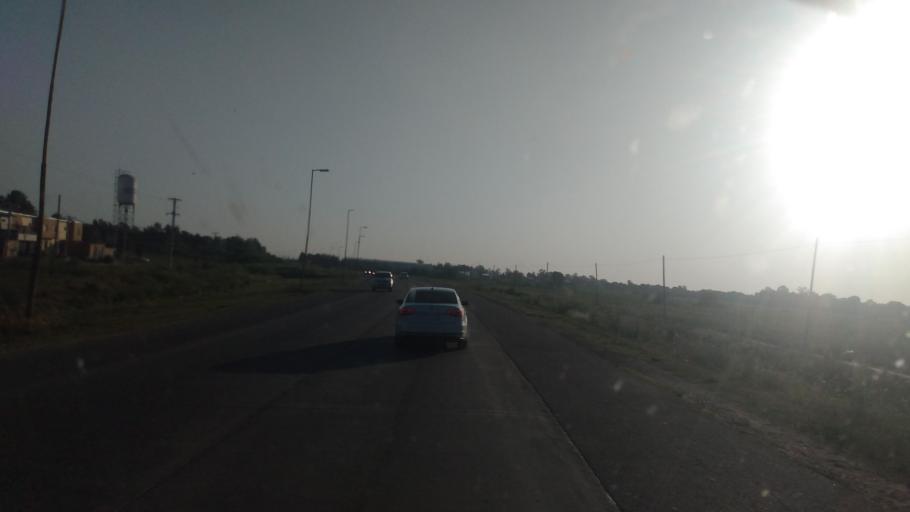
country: AR
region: Buenos Aires
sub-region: Partido de Campana
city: Campana
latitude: -34.1930
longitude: -58.9496
